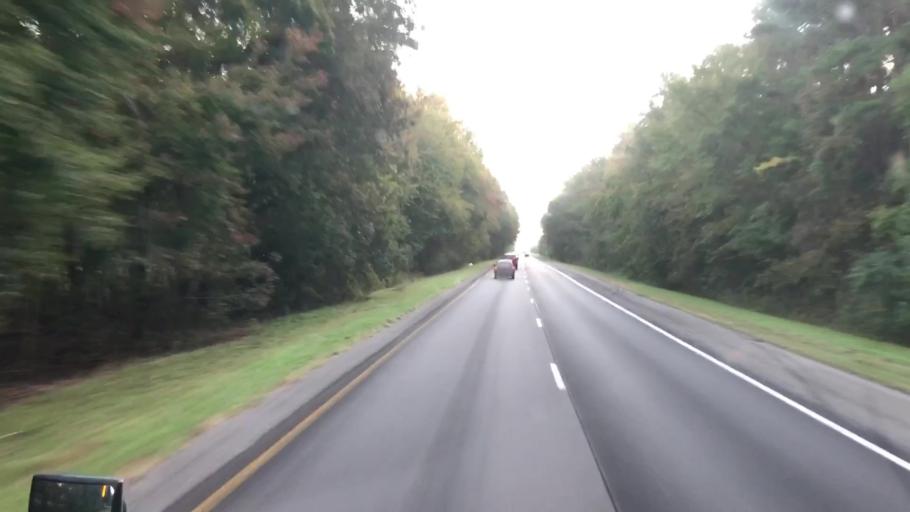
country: US
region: South Carolina
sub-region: Clarendon County
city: Manning
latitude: 33.5690
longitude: -80.3861
